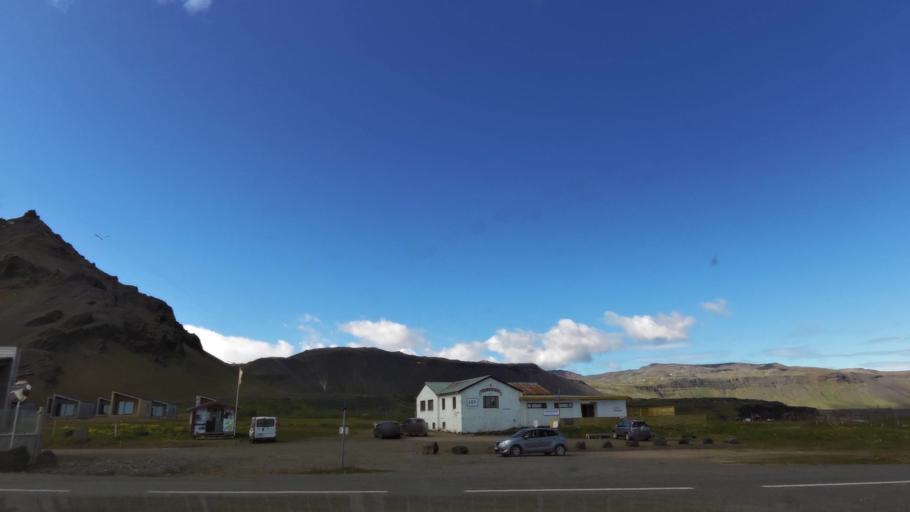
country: IS
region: West
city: Olafsvik
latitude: 64.7669
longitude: -23.6295
